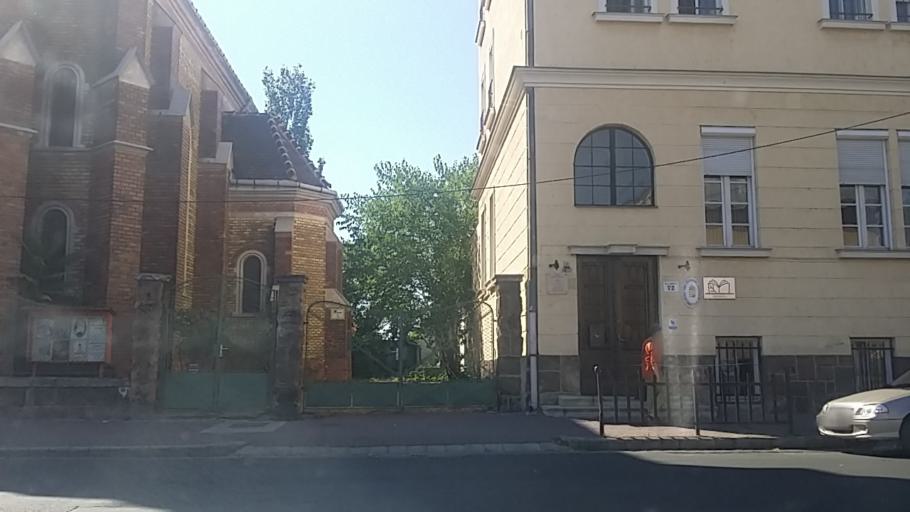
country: HU
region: Budapest
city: Budapest IV. keruelet
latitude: 47.5715
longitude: 19.0873
